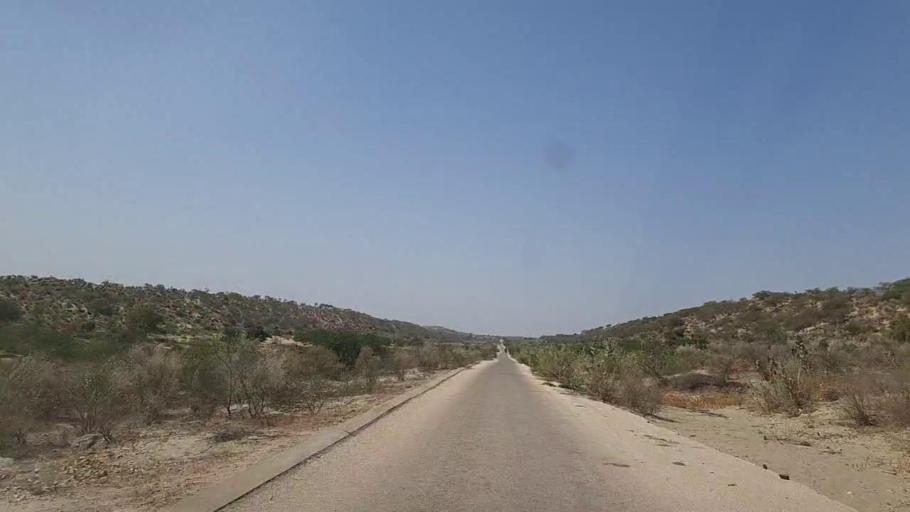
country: PK
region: Sindh
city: Diplo
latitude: 24.5173
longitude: 69.3448
